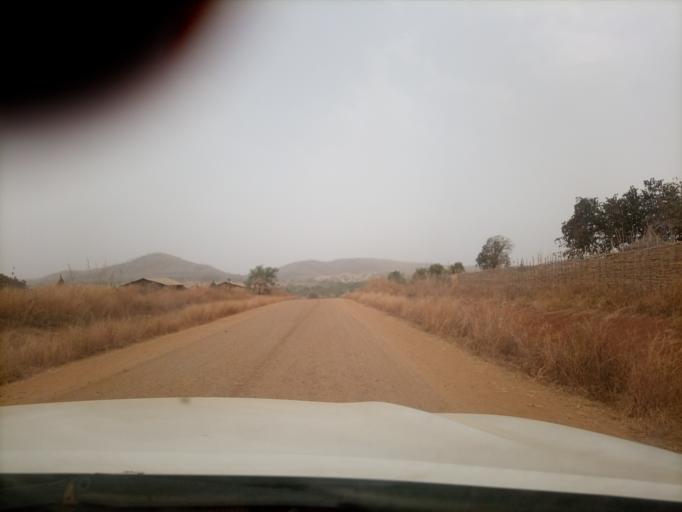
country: ET
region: Oromiya
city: Mendi
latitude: 10.2025
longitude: 35.0899
